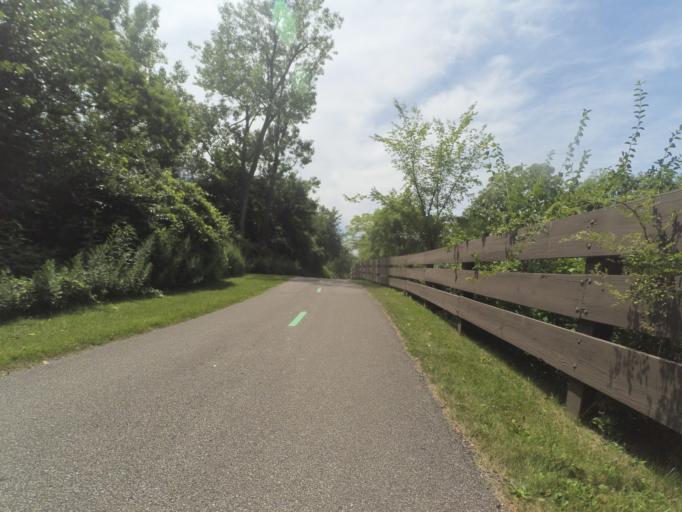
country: US
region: Ohio
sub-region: Cuyahoga County
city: Newburgh Heights
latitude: 41.4214
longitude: -81.6548
